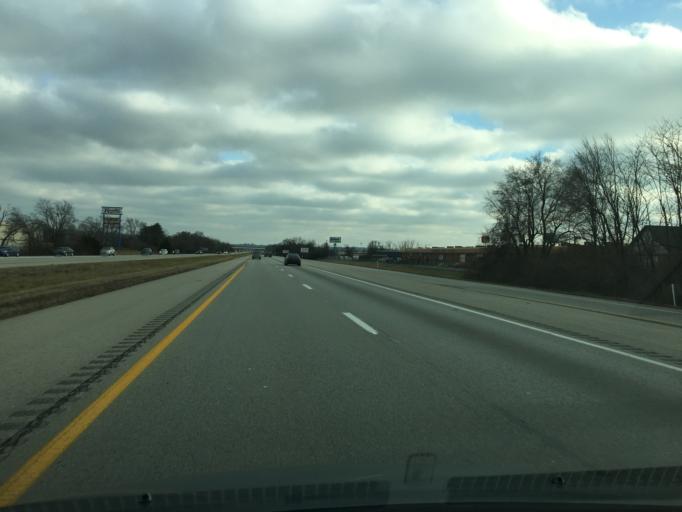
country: US
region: Ohio
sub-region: Hamilton County
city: Harrison
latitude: 39.2589
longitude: -84.7970
